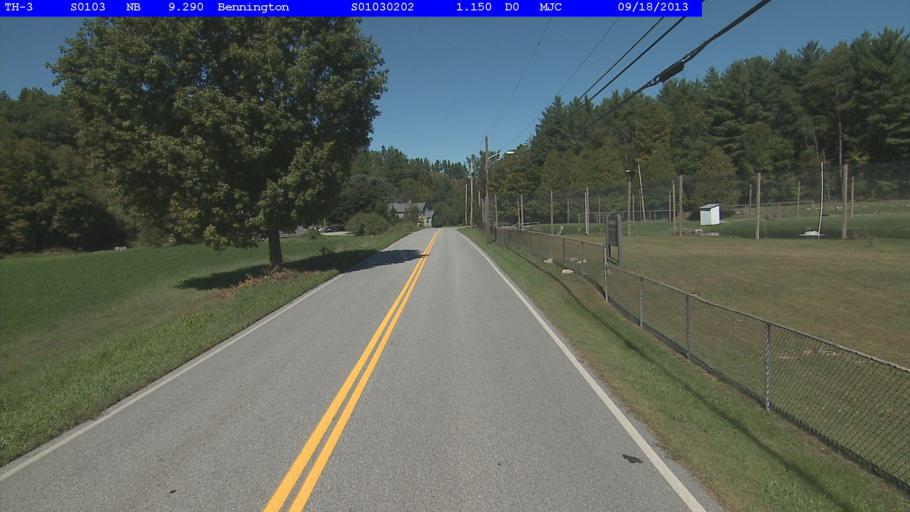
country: US
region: Vermont
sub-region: Bennington County
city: Bennington
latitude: 42.8532
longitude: -73.1737
